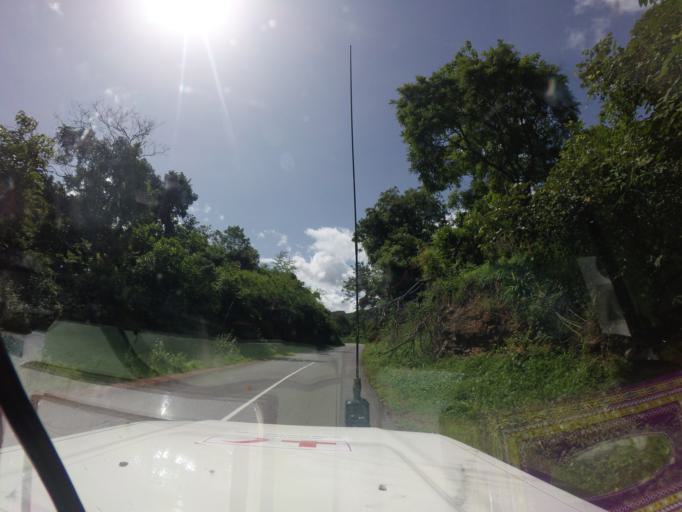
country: GN
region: Mamou
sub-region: Mamou Prefecture
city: Mamou
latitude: 10.2579
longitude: -11.8900
